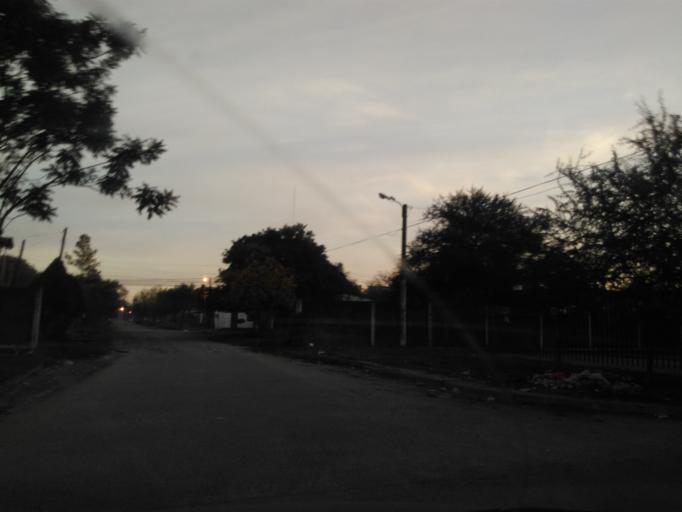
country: AR
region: Chaco
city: Resistencia
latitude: -27.4762
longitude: -58.9888
